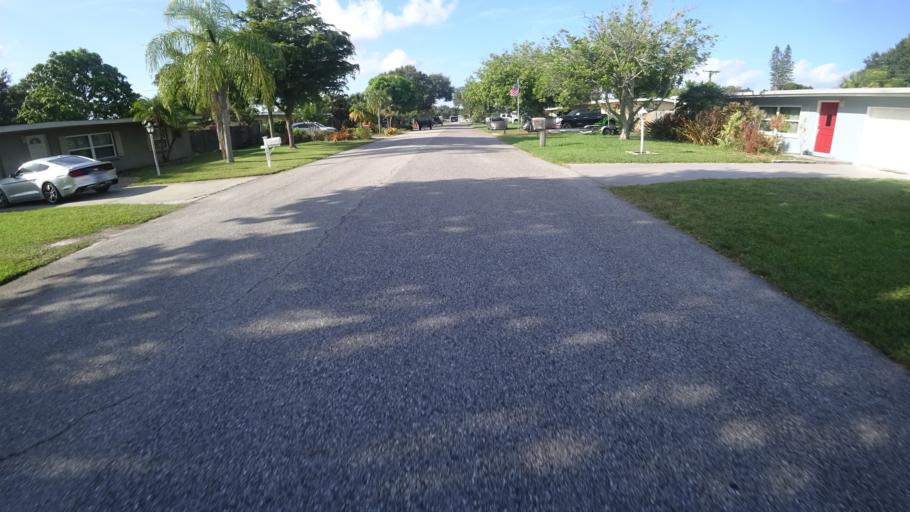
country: US
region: Florida
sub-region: Manatee County
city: West Samoset
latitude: 27.4455
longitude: -82.5595
